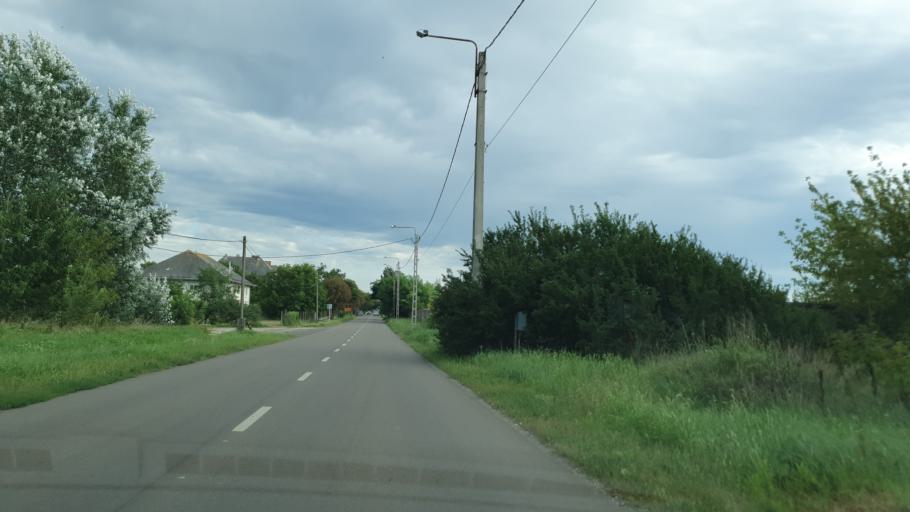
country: HU
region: Heves
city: Zagyvaszanto
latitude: 47.7683
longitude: 19.6704
